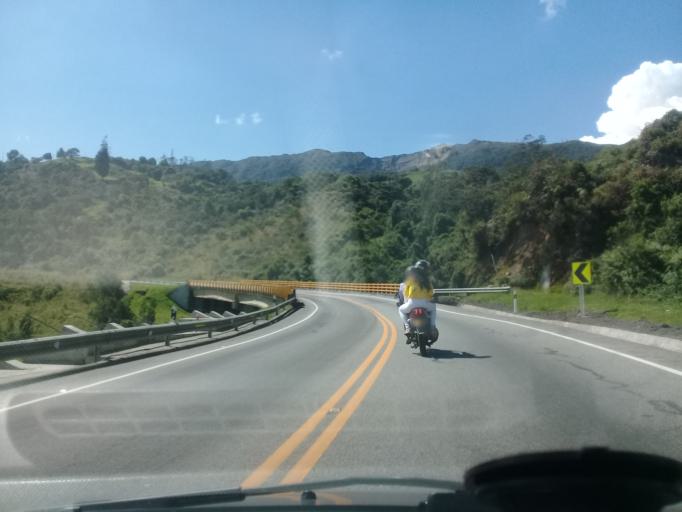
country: CO
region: Cundinamarca
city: Chipaque
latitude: 4.4542
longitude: -74.0624
